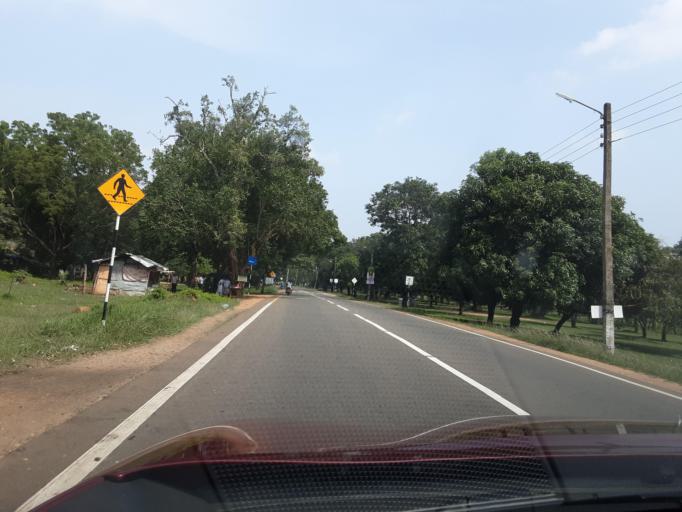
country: LK
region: North Central
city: Anuradhapura
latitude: 8.3547
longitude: 80.5099
